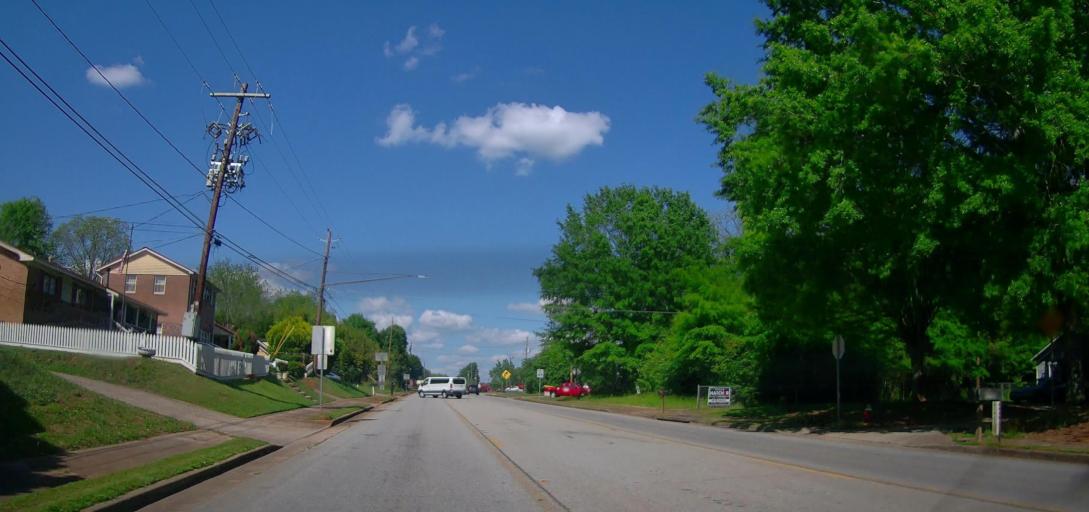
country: US
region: Georgia
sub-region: Morgan County
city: Madison
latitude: 33.6063
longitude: -83.4562
